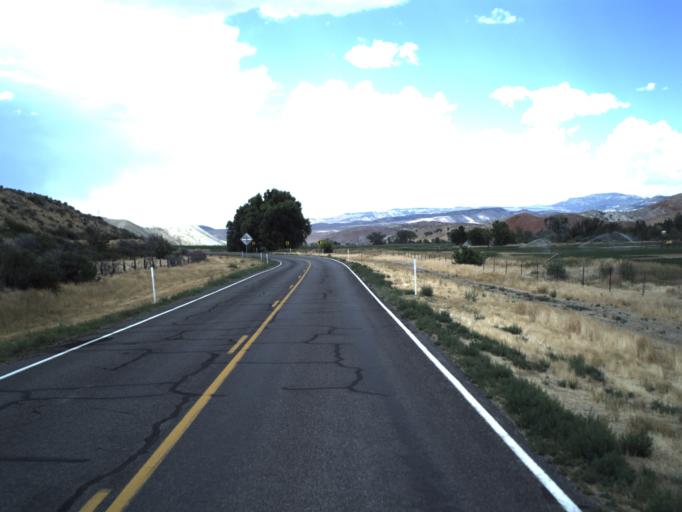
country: US
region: Utah
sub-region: Sanpete County
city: Centerfield
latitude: 39.1219
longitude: -111.7149
